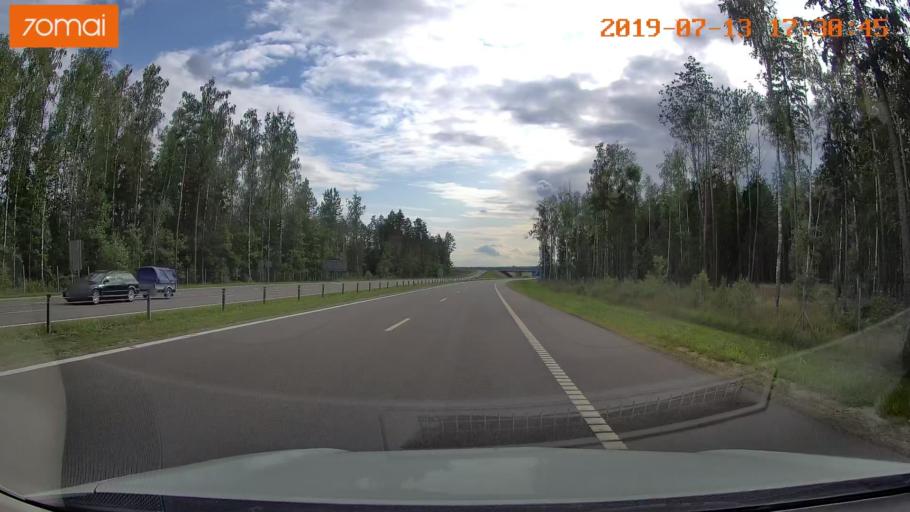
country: BY
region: Mogilev
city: Babruysk
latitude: 53.2134
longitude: 29.0777
